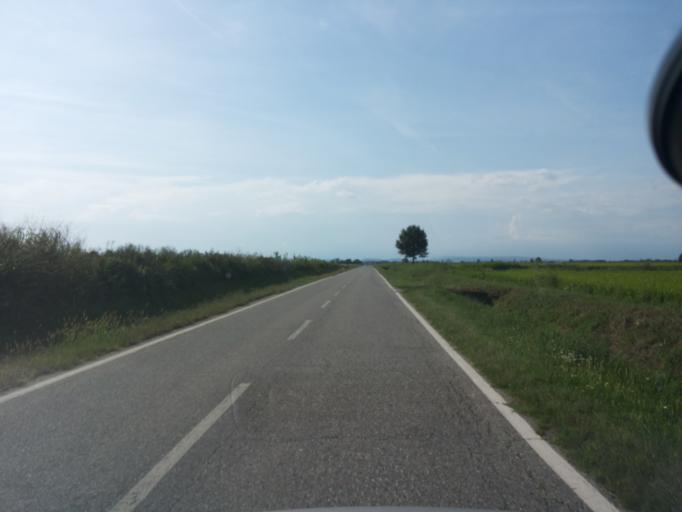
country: IT
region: Piedmont
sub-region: Provincia di Vercelli
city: Salasco
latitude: 45.3034
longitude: 8.2597
